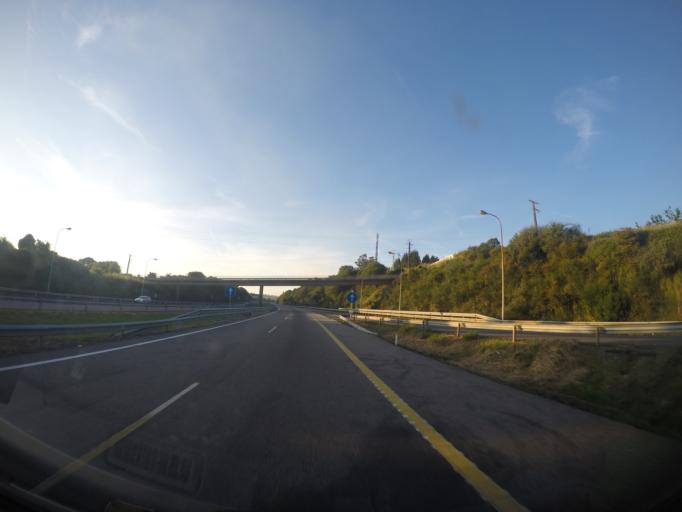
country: ES
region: Aragon
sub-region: Provincia de Zaragoza
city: Bujaraloz
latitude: 41.5286
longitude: -0.2030
